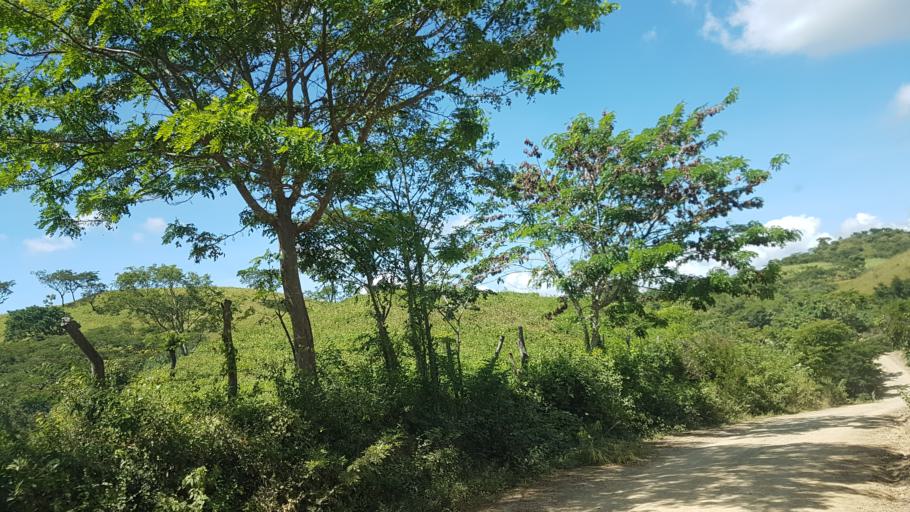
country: HN
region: El Paraiso
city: Santa Cruz
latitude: 13.7314
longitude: -86.6910
